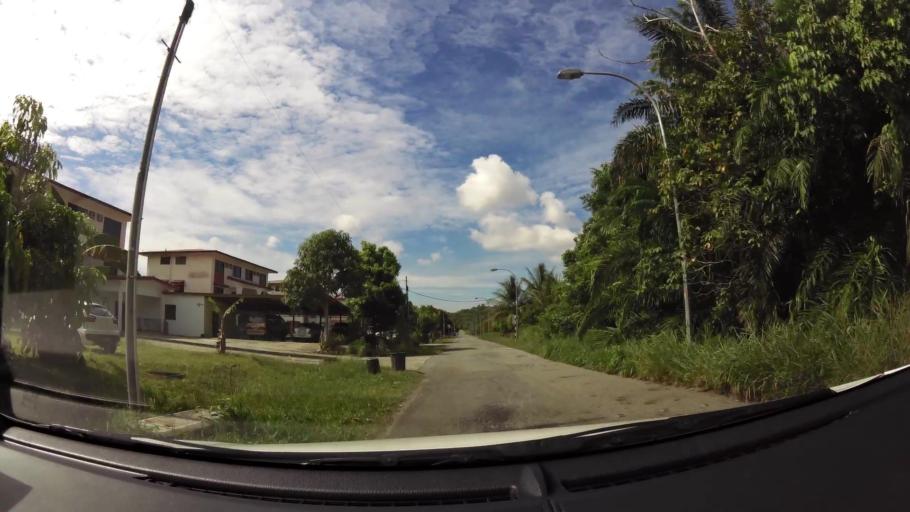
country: BN
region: Brunei and Muara
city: Bandar Seri Begawan
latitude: 4.9351
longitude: 114.9091
